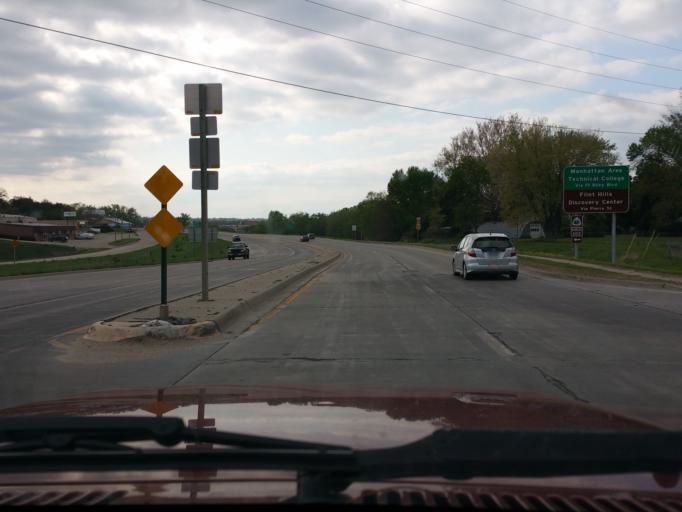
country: US
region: Kansas
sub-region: Riley County
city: Manhattan
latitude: 39.1726
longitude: -96.5466
